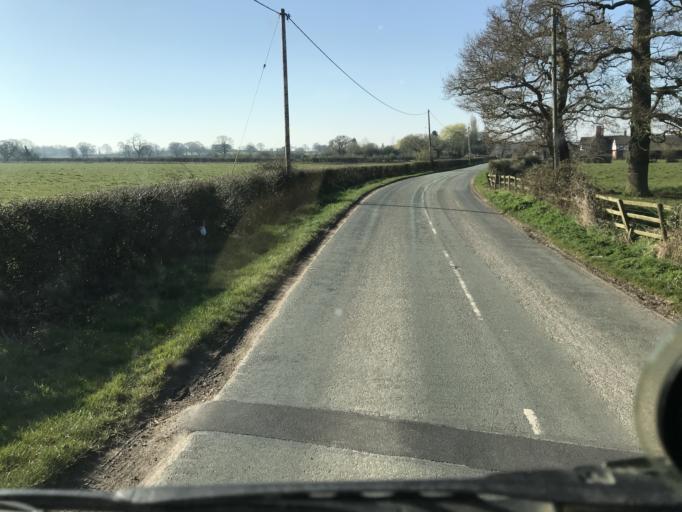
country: GB
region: England
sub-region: Cheshire West and Chester
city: Waverton
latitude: 53.1634
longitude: -2.8257
